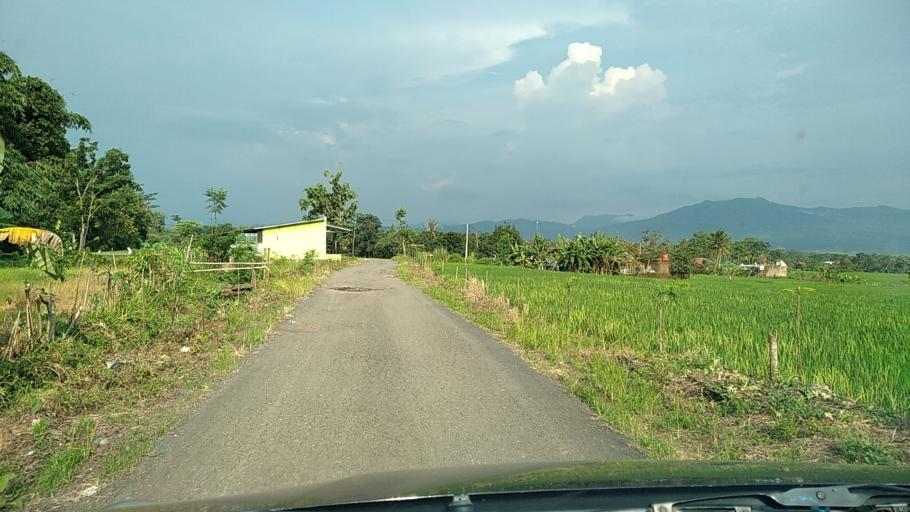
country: ID
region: Central Java
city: Randudongkal
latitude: -7.0769
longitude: 109.3389
